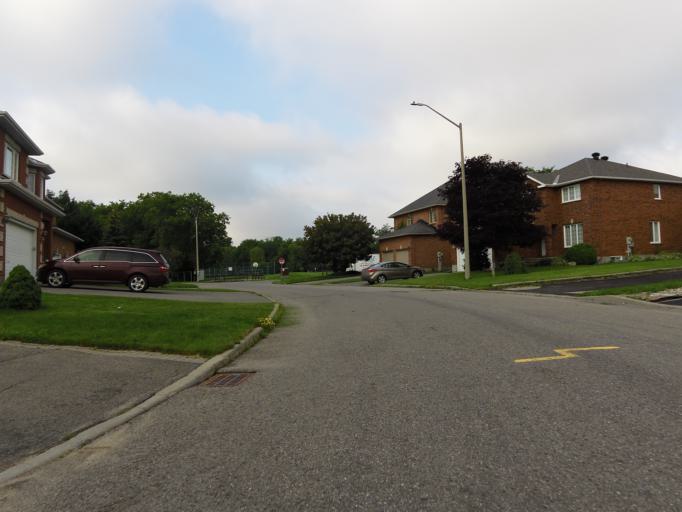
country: CA
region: Ontario
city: Ottawa
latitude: 45.3464
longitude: -75.6589
